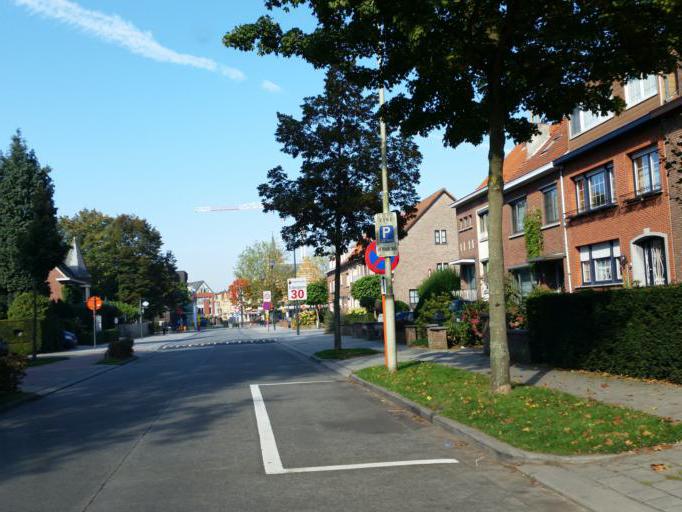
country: BE
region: Flanders
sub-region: Provincie Antwerpen
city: Edegem
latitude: 51.1533
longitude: 4.4463
